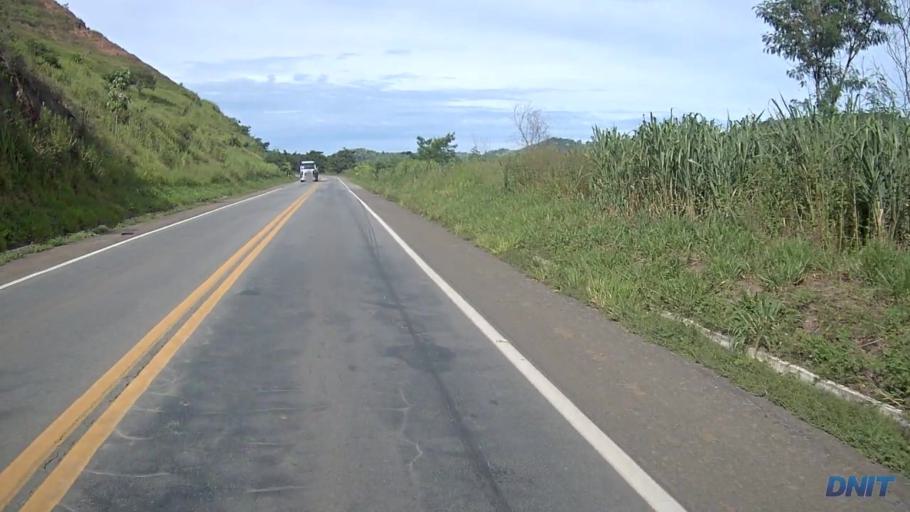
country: BR
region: Minas Gerais
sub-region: Belo Oriente
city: Belo Oriente
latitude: -19.1726
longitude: -42.2520
